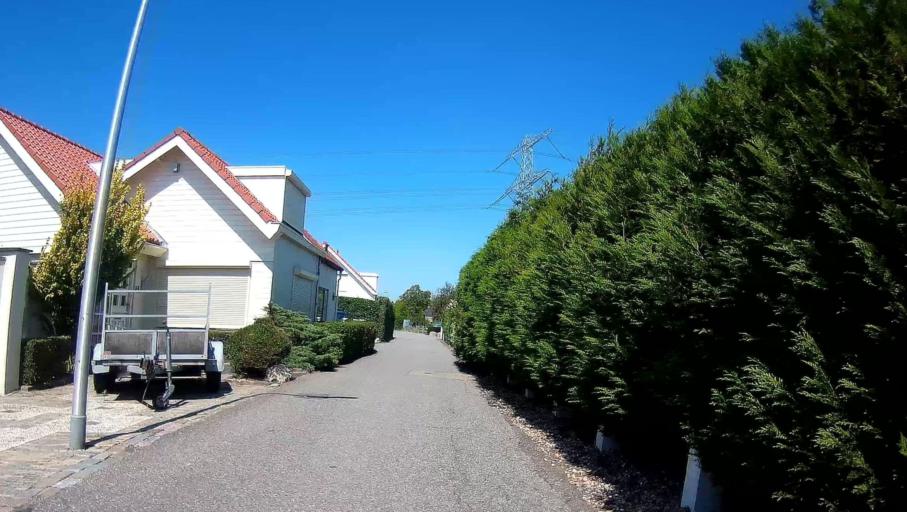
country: NL
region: South Holland
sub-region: Gemeente Westland
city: Maasdijk
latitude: 51.9725
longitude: 4.2109
